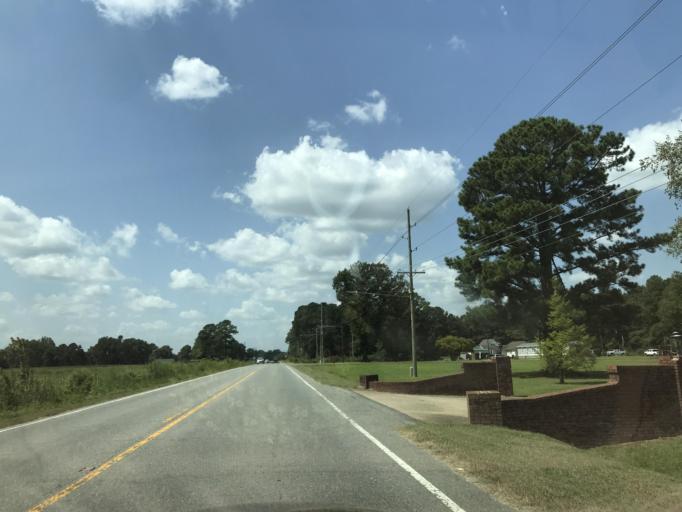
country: US
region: North Carolina
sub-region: Sampson County
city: Plain View
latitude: 35.2473
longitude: -78.3617
